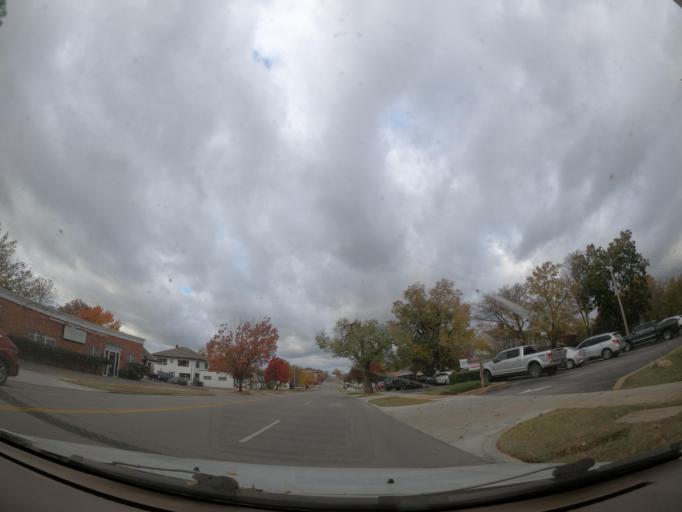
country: US
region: Oklahoma
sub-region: Tulsa County
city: Tulsa
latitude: 36.1406
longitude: -95.9611
